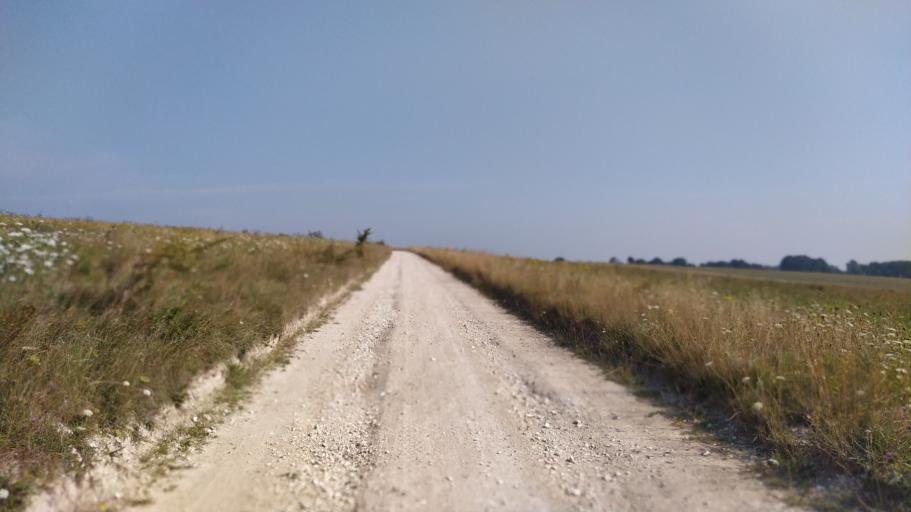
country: GB
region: England
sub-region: Wiltshire
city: Shrewton
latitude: 51.1823
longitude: -1.9510
